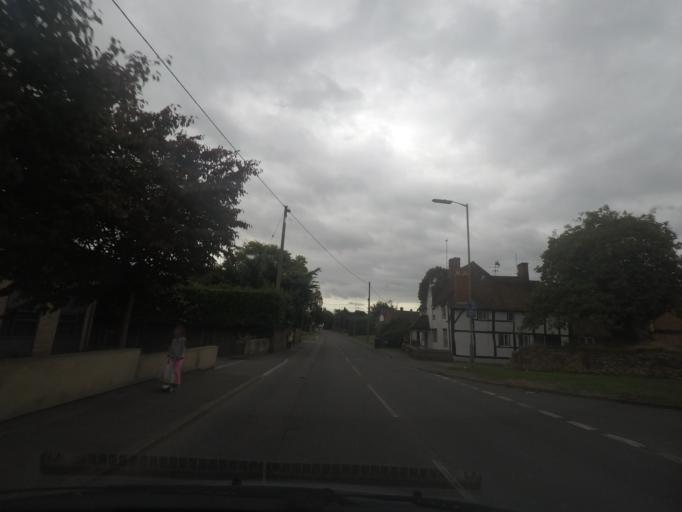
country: GB
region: England
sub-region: Oxfordshire
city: Didcot
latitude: 51.6096
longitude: -1.2528
